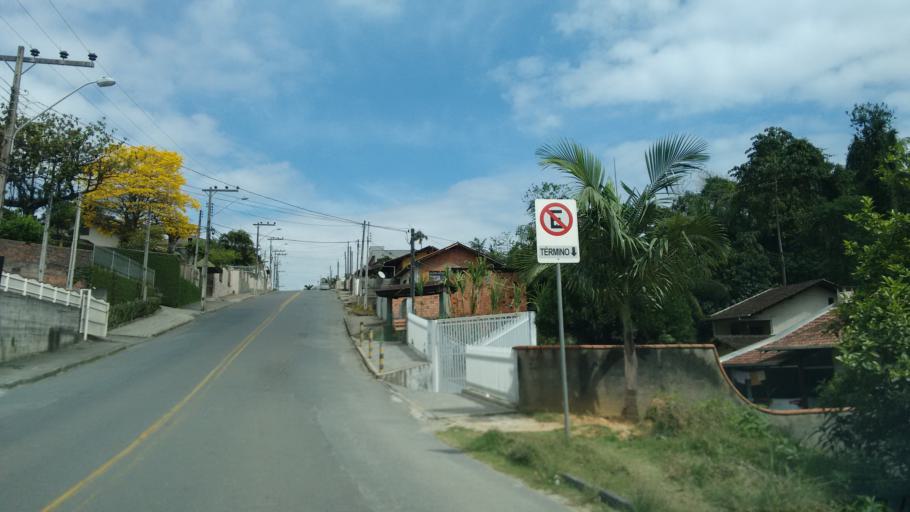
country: BR
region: Santa Catarina
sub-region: Blumenau
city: Blumenau
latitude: -26.8594
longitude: -49.1261
